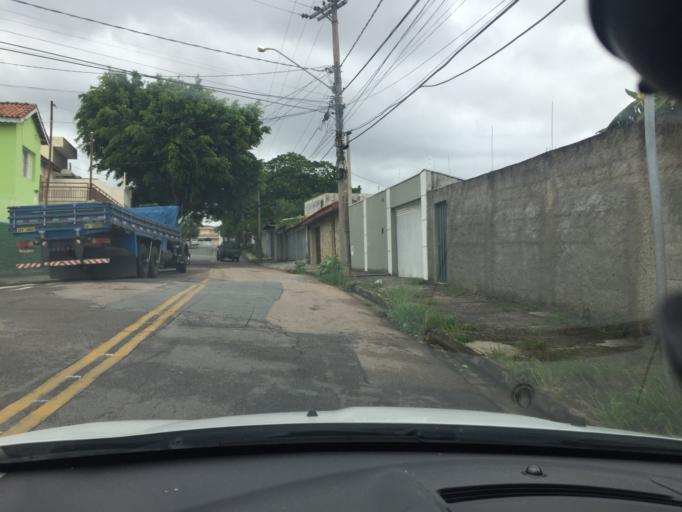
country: BR
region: Sao Paulo
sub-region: Jundiai
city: Jundiai
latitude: -23.1742
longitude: -46.8782
